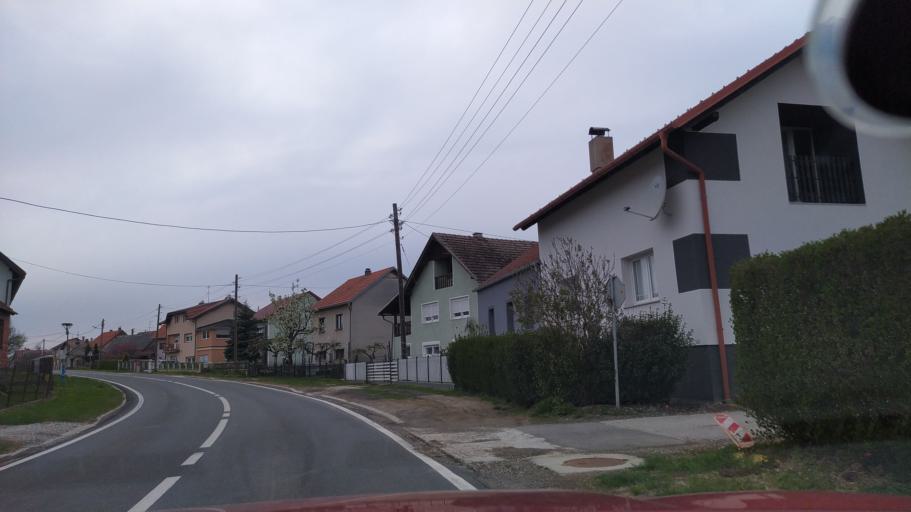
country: HR
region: Varazdinska
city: Jalzabet
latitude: 46.2105
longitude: 16.4595
